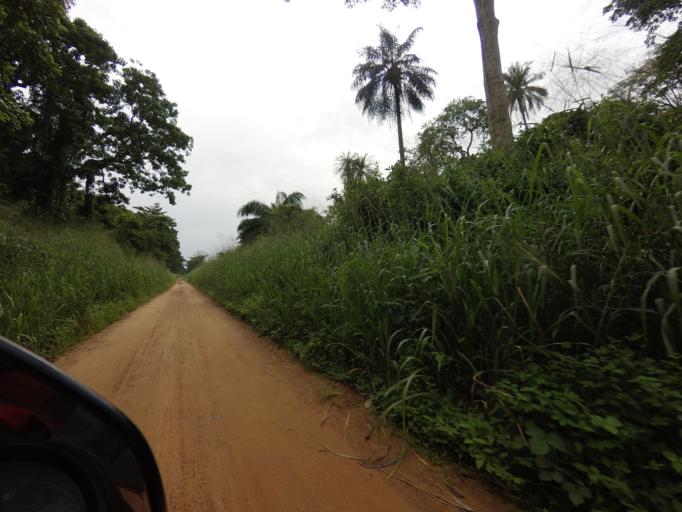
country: SL
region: Eastern Province
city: Jojoima
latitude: 7.9294
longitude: -10.7650
